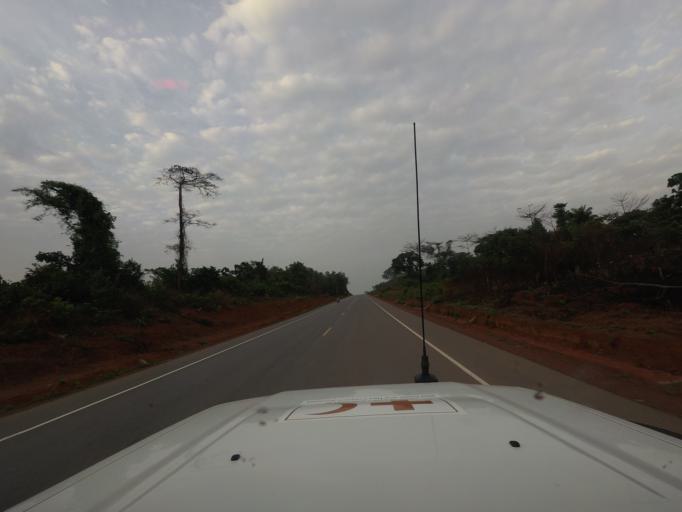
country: LR
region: Nimba
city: Sanniquellie
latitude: 7.1913
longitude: -9.0223
